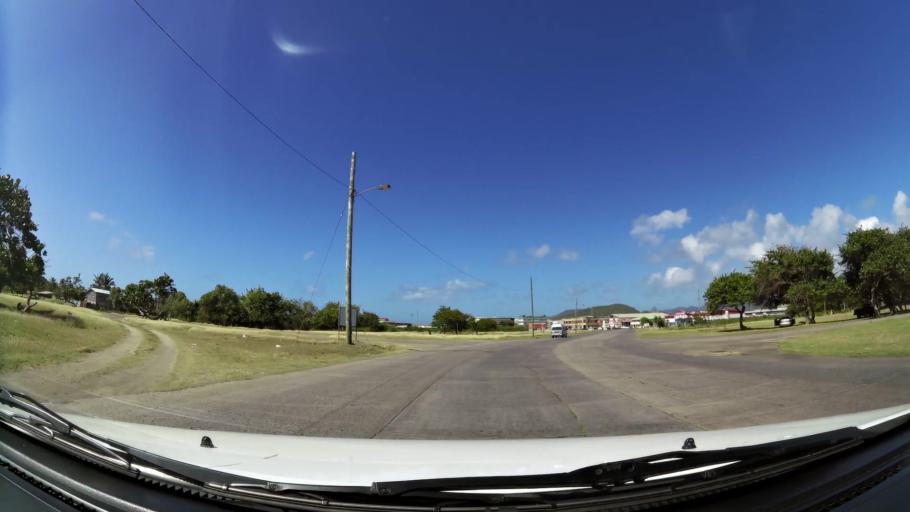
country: LC
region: Vieux-Fort
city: Vieux Fort
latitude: 13.7283
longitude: -60.9459
